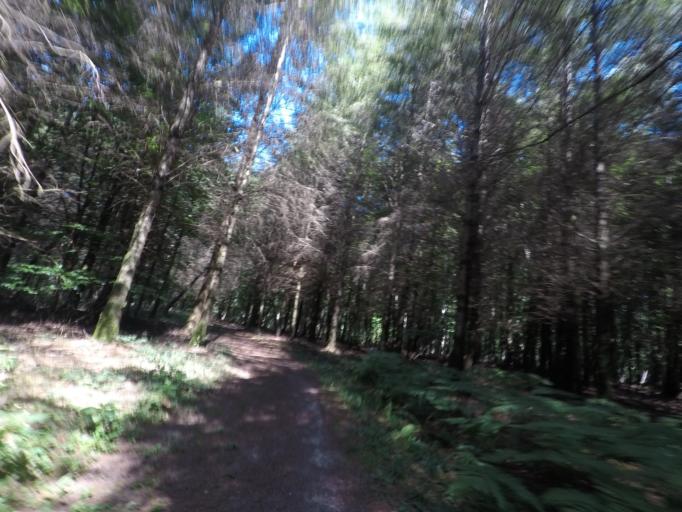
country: LU
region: Luxembourg
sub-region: Canton de Capellen
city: Kopstal
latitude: 49.6480
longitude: 6.0667
